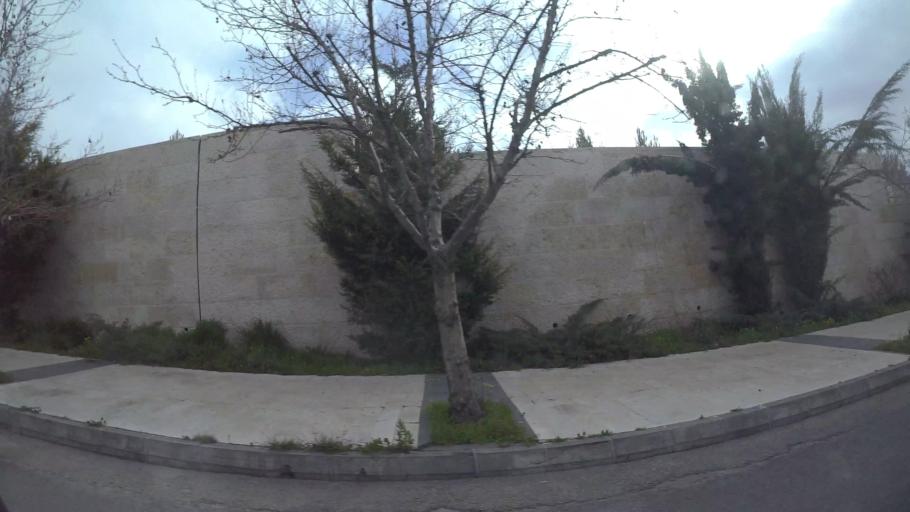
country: JO
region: Amman
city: Wadi as Sir
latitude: 31.9843
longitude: 35.8209
